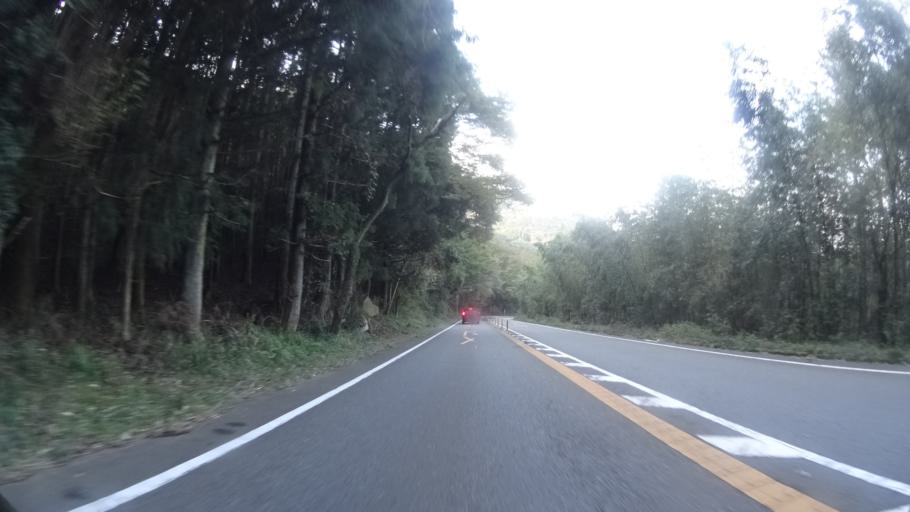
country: JP
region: Oita
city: Beppu
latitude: 33.2722
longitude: 131.4433
